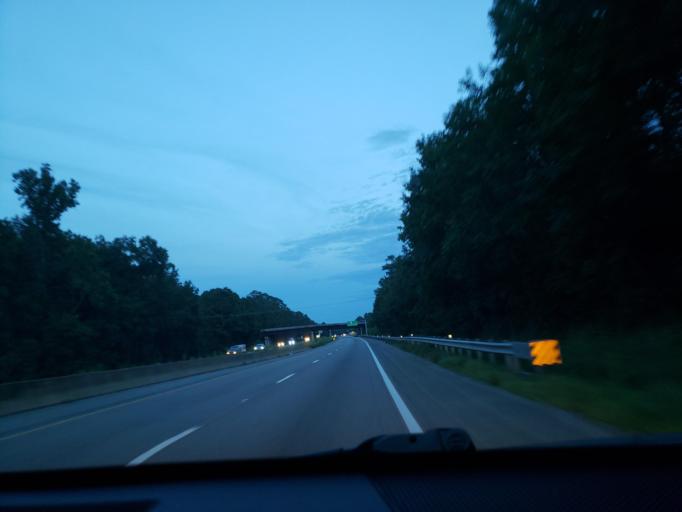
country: US
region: Virginia
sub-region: City of Franklin
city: Franklin
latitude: 36.6493
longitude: -76.9149
